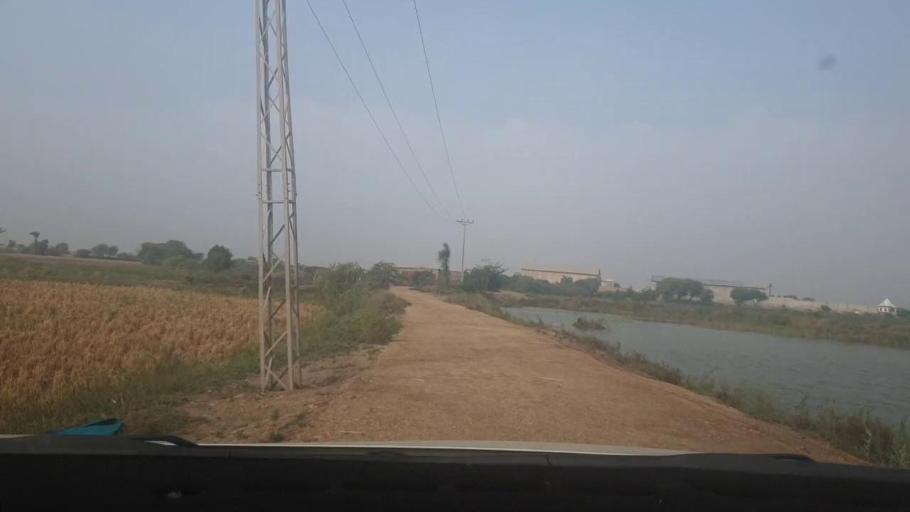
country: PK
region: Sindh
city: Tando Muhammad Khan
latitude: 25.1087
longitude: 68.5400
